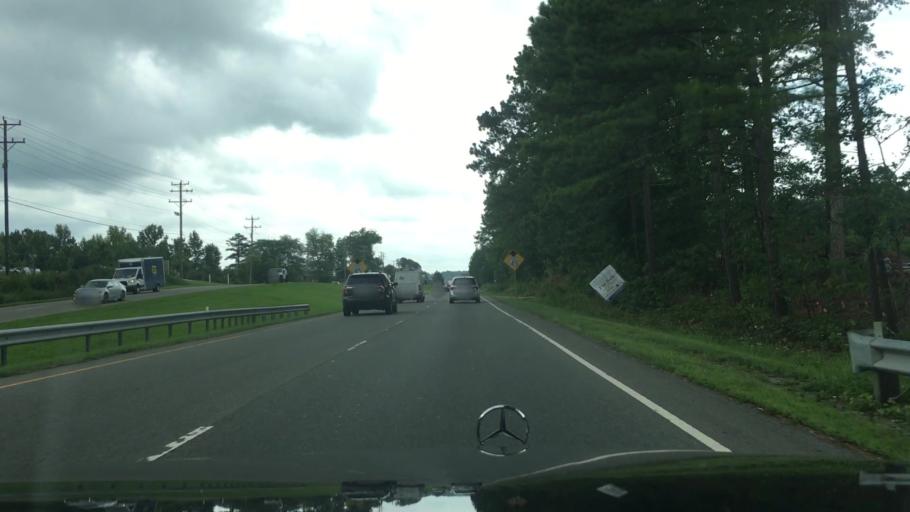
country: US
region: Virginia
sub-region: Chesterfield County
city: Woodlake
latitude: 37.4021
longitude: -77.6958
